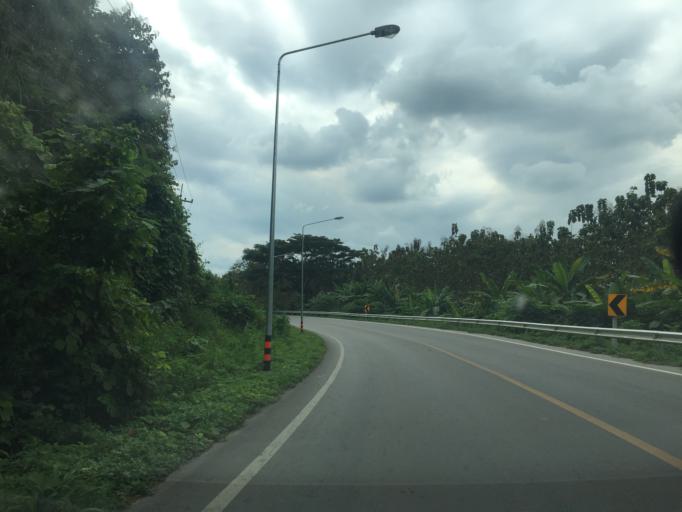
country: TH
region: Lampang
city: Lampang
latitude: 18.4721
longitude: 99.4647
